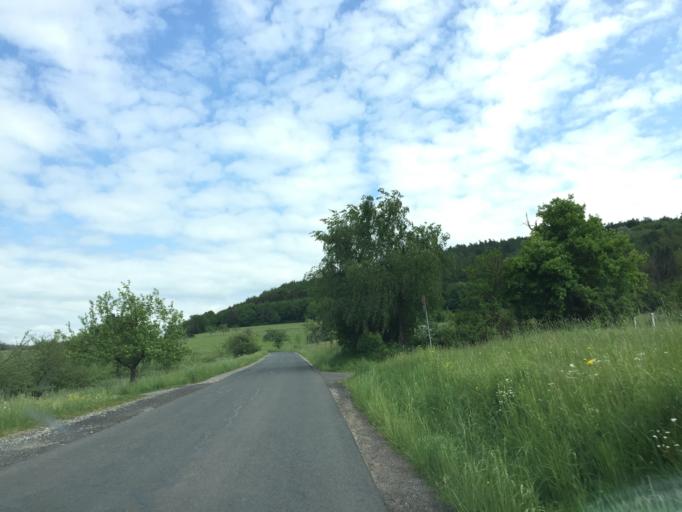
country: DE
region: Bavaria
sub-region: Regierungsbezirk Unterfranken
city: Haibach
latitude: 49.9638
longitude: 9.2545
